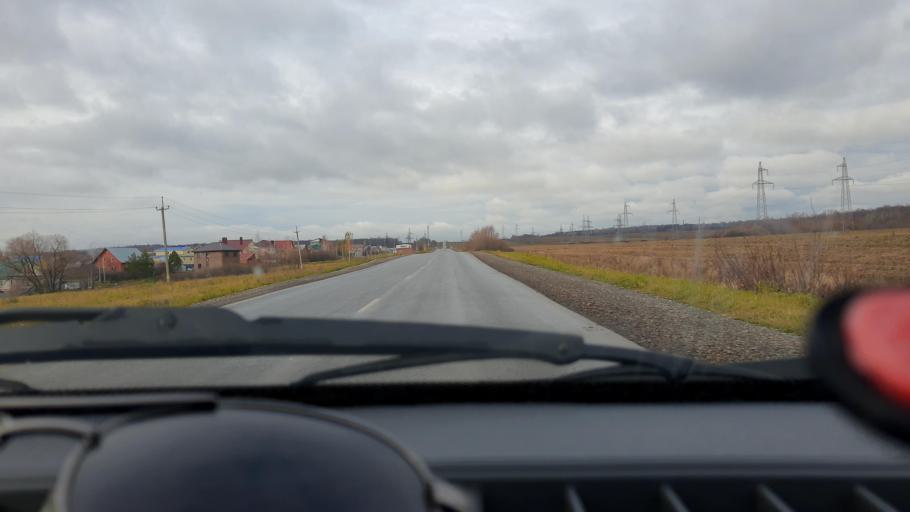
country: RU
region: Bashkortostan
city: Mikhaylovka
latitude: 54.8320
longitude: 55.9192
